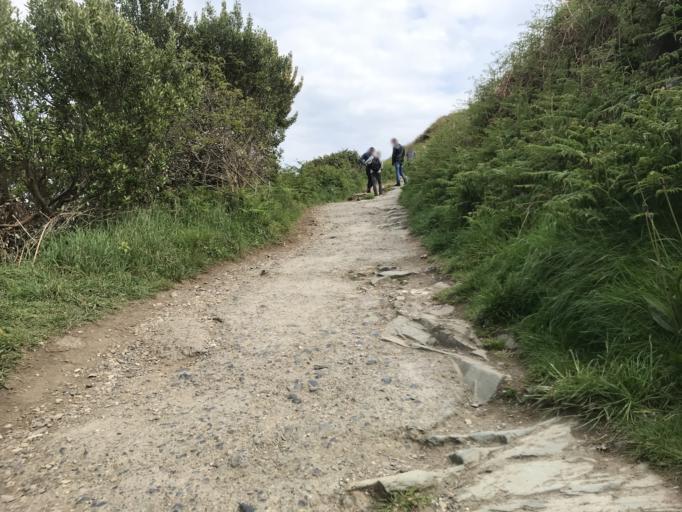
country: IE
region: Leinster
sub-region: Fingal County
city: Howth
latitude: 53.3855
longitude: -6.0494
